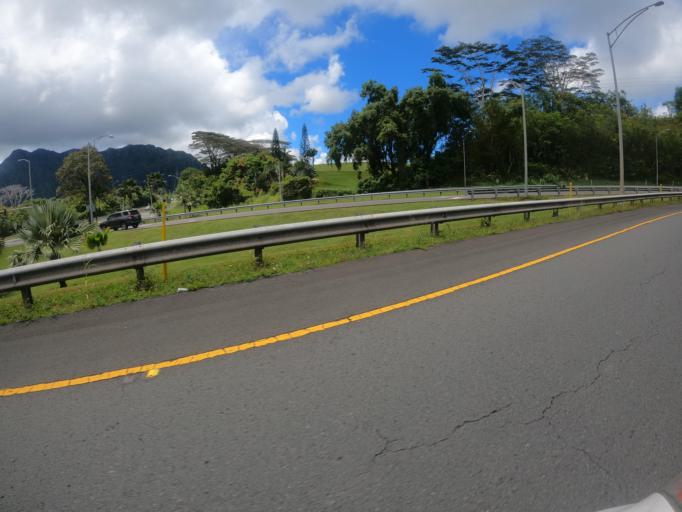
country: US
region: Hawaii
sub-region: Honolulu County
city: Maunawili
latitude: 21.3859
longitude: -157.7909
